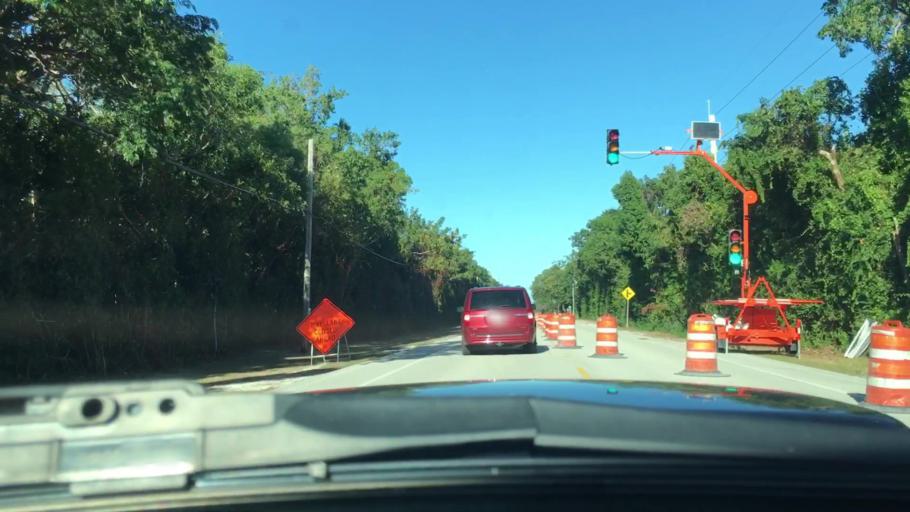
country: US
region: Florida
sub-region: Monroe County
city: North Key Largo
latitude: 25.1892
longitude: -80.3583
